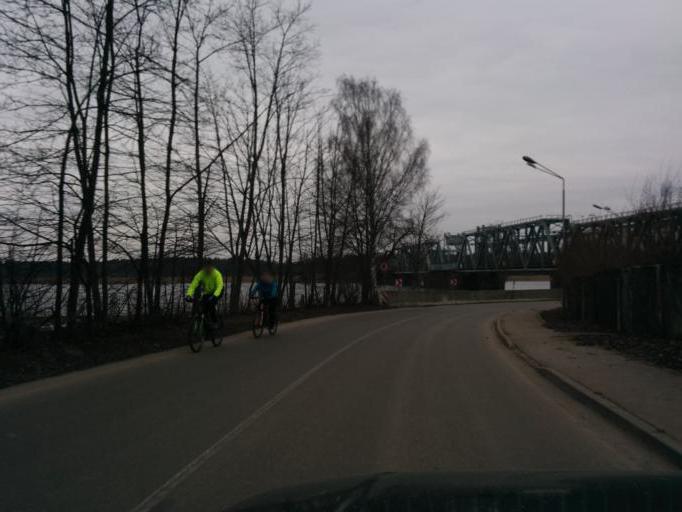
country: LV
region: Babite
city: Pinki
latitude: 56.9807
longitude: 23.8746
